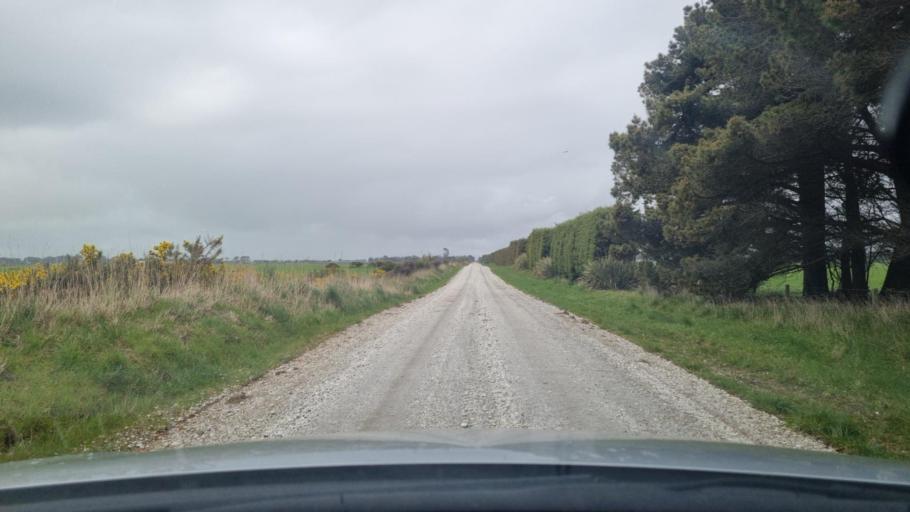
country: NZ
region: Southland
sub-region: Invercargill City
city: Invercargill
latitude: -46.5008
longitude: 168.4088
